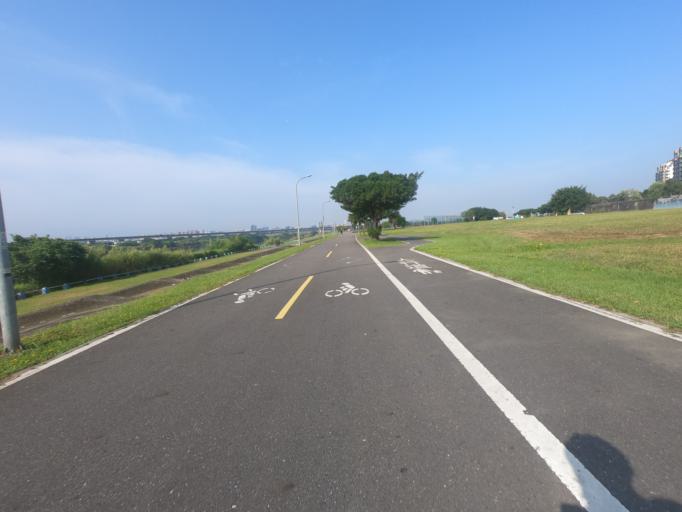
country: TW
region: Taipei
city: Taipei
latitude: 25.0761
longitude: 121.5674
